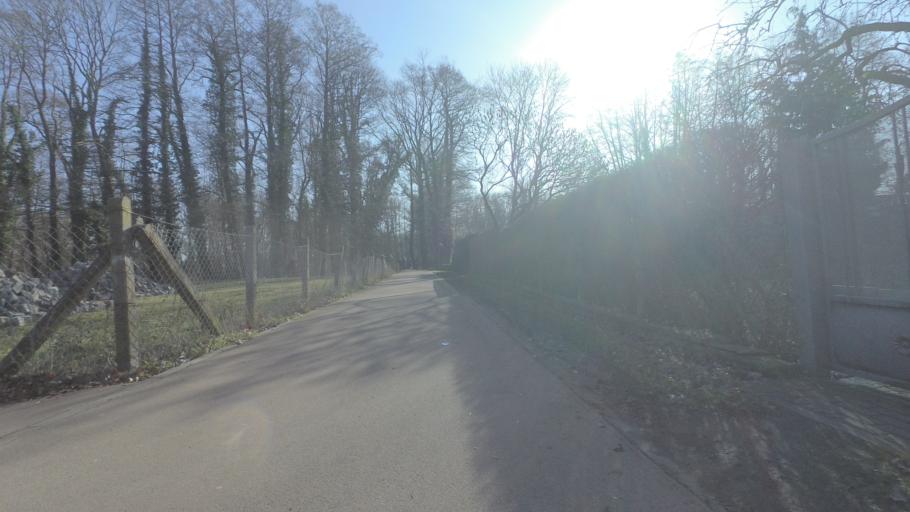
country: DE
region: Brandenburg
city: Luckenwalde
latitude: 52.0837
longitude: 13.1736
